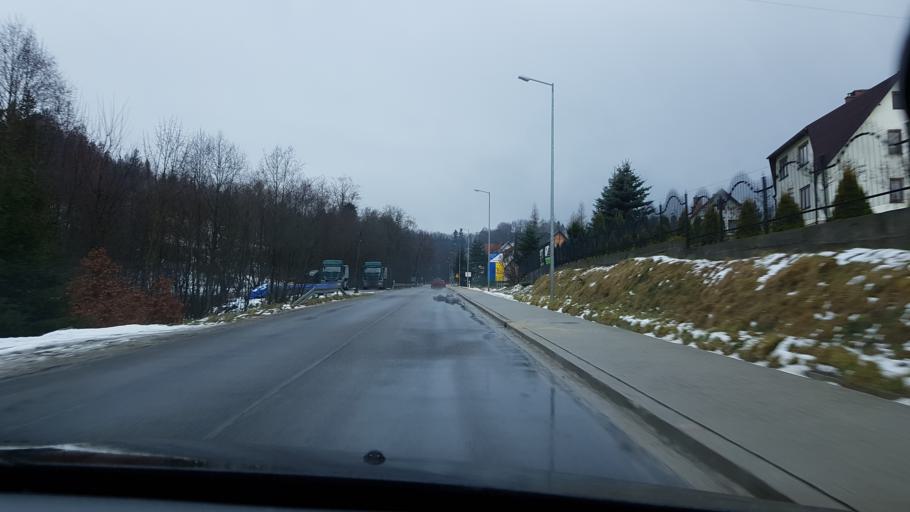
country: PL
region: Lesser Poland Voivodeship
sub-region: Powiat nowotarski
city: Raba Wyzna
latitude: 49.5399
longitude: 19.8909
